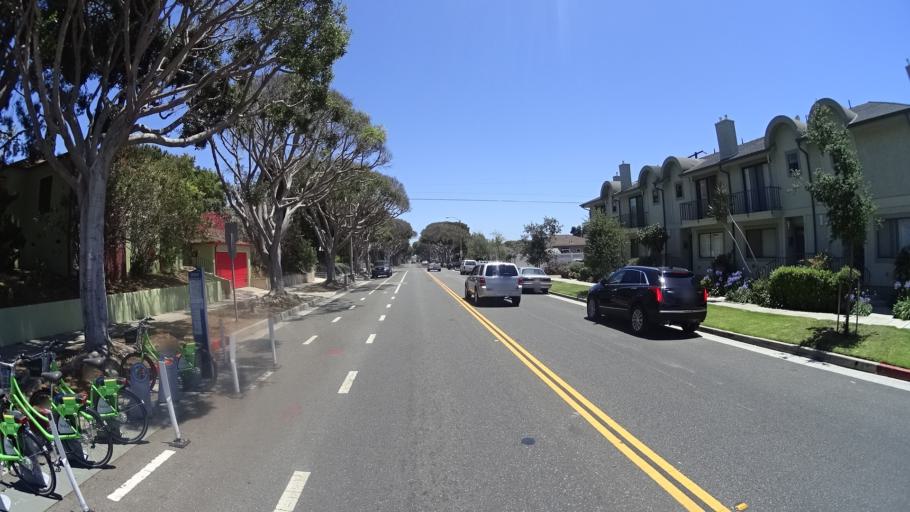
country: US
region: California
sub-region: Los Angeles County
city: Santa Monica
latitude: 34.0111
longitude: -118.4765
